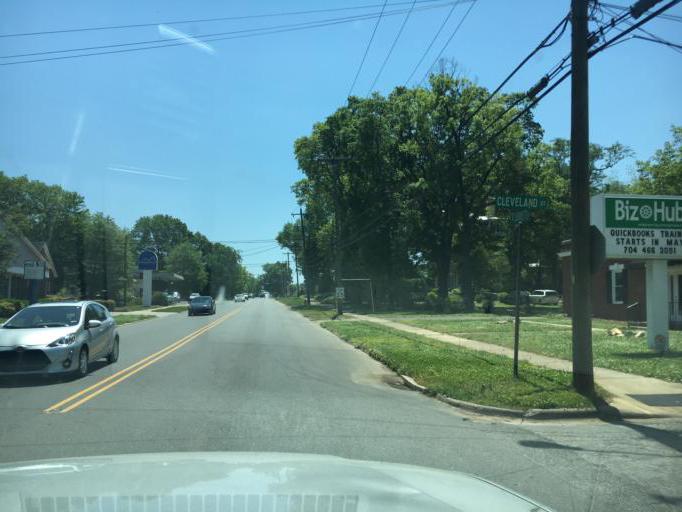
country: US
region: North Carolina
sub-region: Cleveland County
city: Shelby
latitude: 35.2970
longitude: -81.5400
